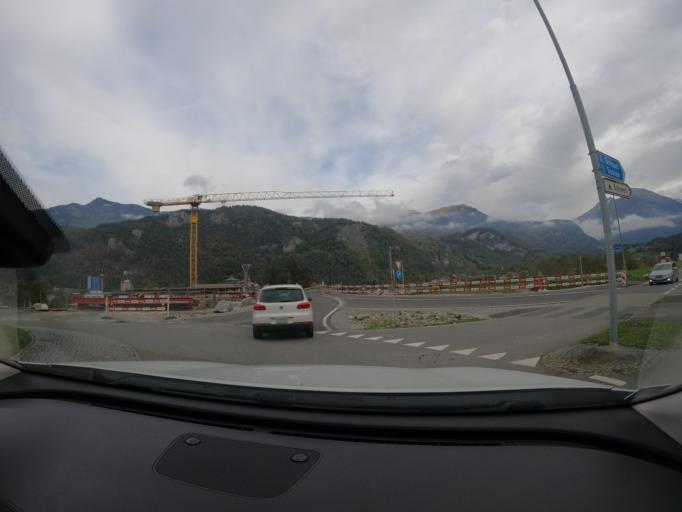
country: CH
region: Bern
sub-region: Interlaken-Oberhasli District
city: Meiringen
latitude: 46.7270
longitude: 8.1704
